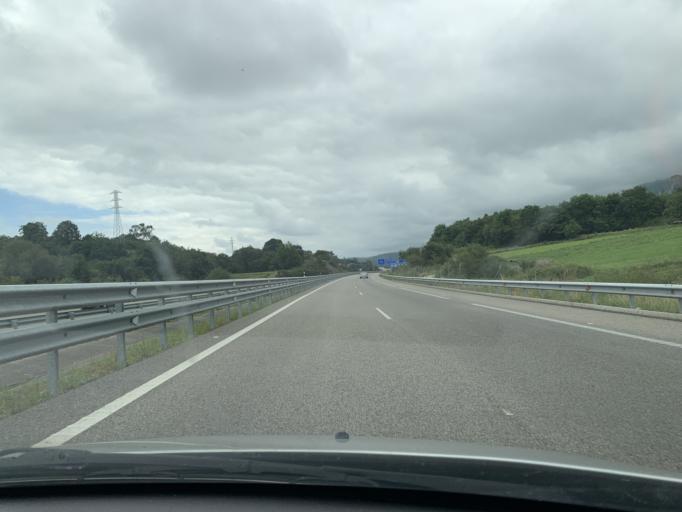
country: ES
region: Asturias
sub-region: Province of Asturias
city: Llanes
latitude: 43.4104
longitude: -4.7742
